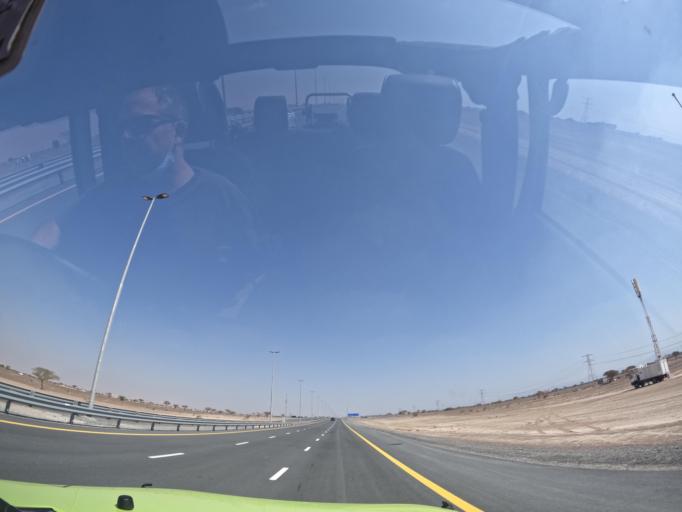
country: AE
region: Ash Shariqah
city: Adh Dhayd
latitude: 24.9496
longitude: 55.8336
